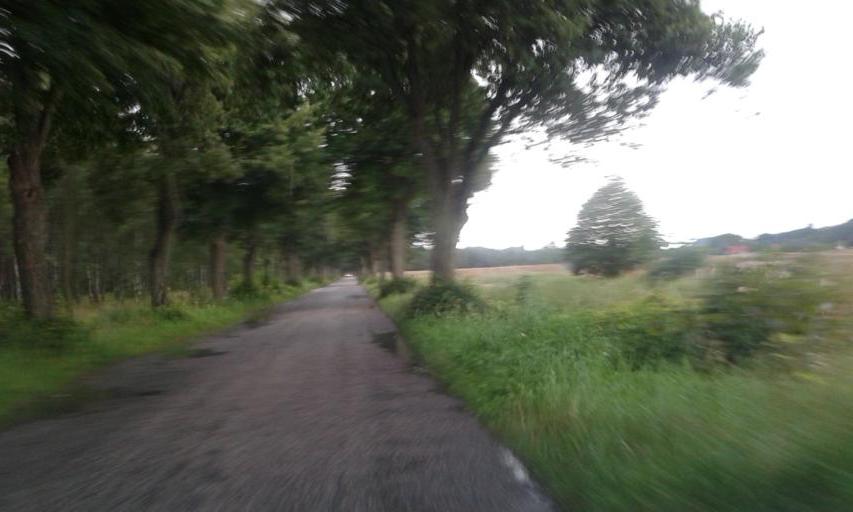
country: PL
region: Greater Poland Voivodeship
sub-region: Powiat zlotowski
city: Sypniewo
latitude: 53.4685
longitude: 16.5085
